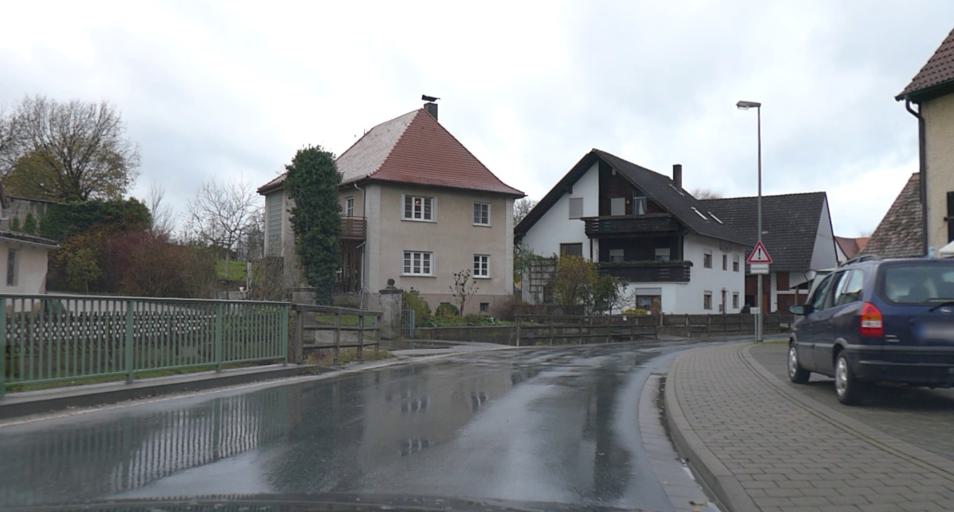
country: DE
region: Bavaria
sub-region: Upper Franconia
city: Leutenbach
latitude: 49.6900
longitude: 11.1700
